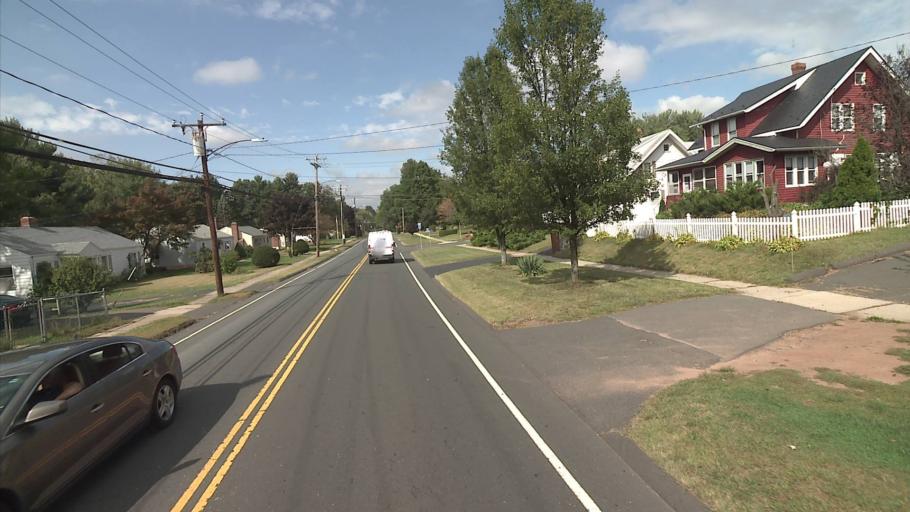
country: US
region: Connecticut
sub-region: Hartford County
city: Newington
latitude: 41.7019
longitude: -72.7248
